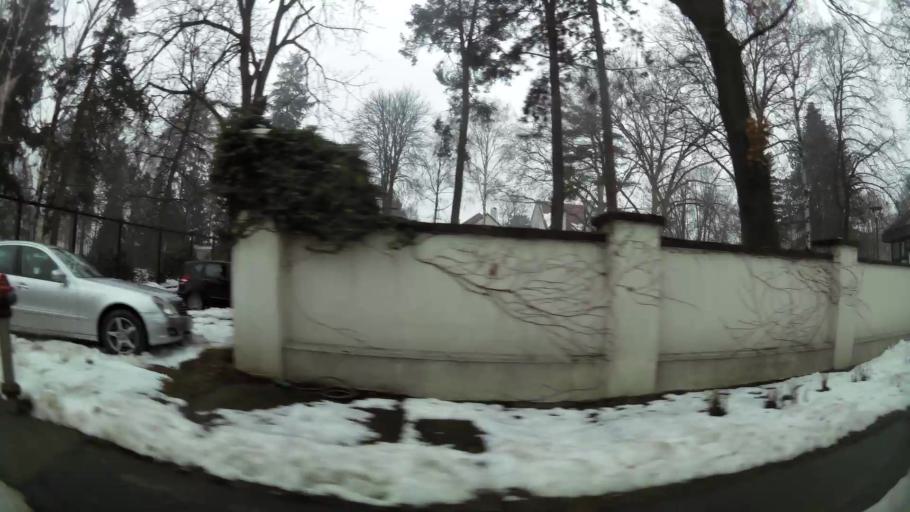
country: RS
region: Central Serbia
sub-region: Belgrade
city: Savski Venac
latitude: 44.7828
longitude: 20.4541
